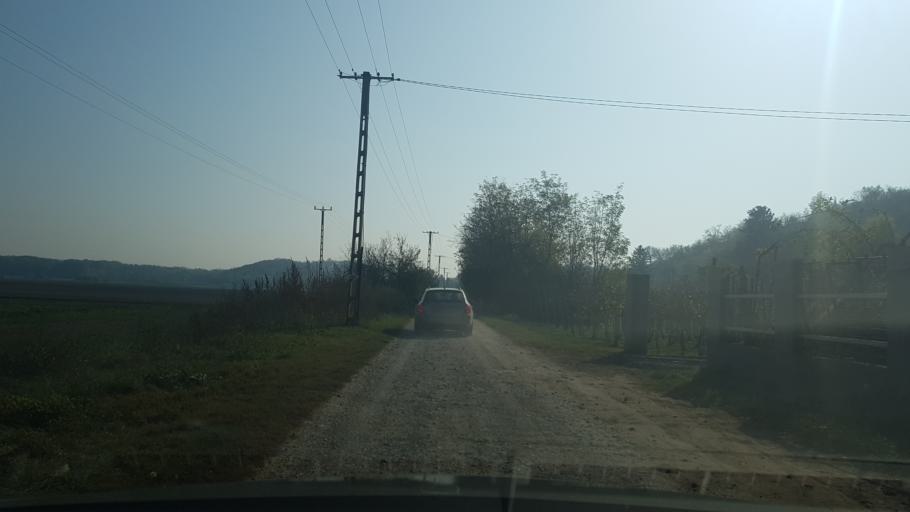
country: HU
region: Fejer
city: Adony
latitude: 47.0792
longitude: 18.8583
